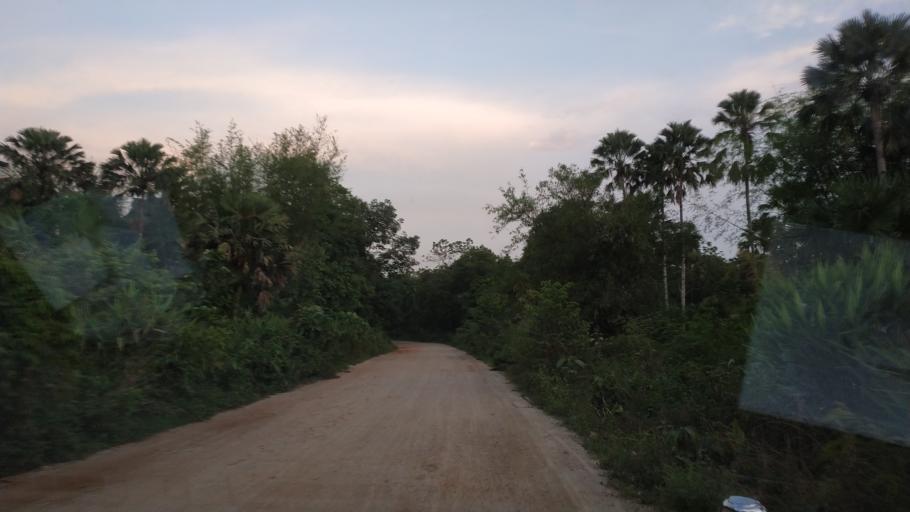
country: MM
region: Mon
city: Kyaikto
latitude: 17.4284
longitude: 97.0433
